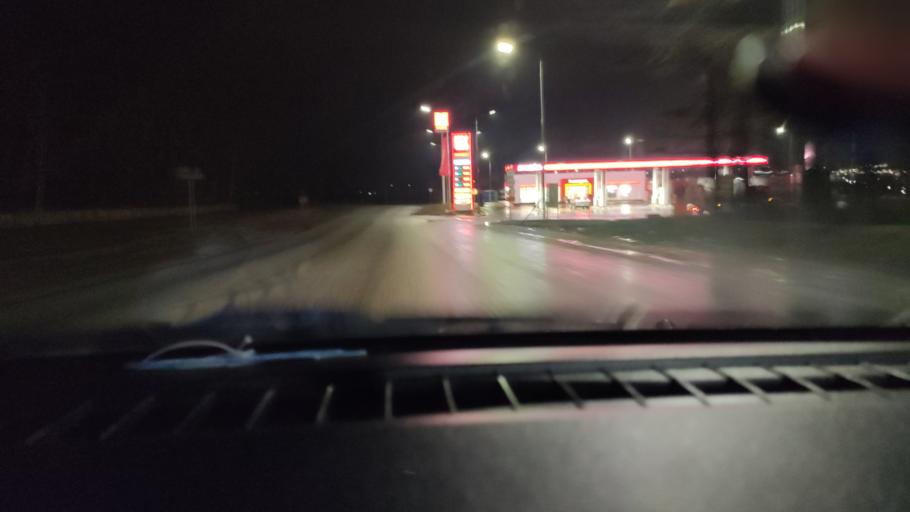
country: RU
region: Udmurtiya
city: Votkinsk
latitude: 57.0295
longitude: 53.9518
